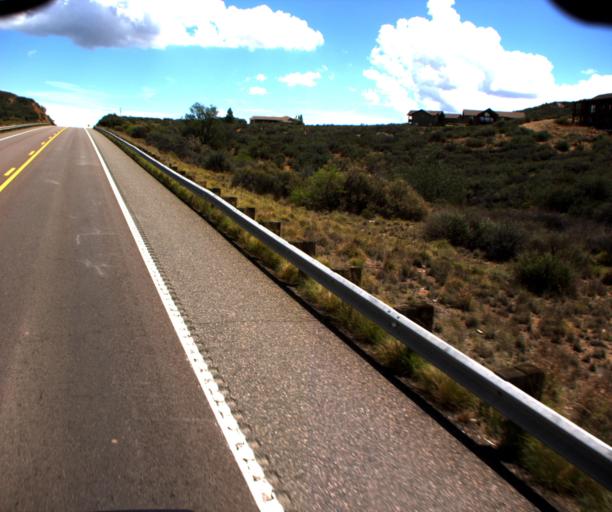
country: US
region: Arizona
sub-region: Yavapai County
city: Dewey-Humboldt
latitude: 34.5428
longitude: -112.1891
